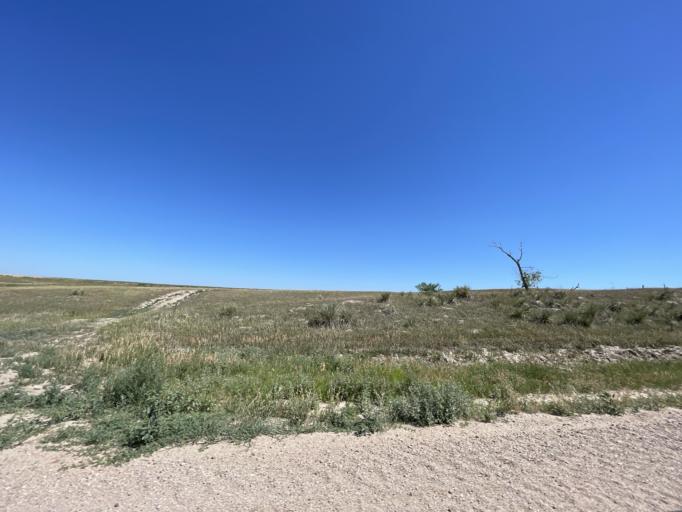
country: US
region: Nebraska
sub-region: Red Willow County
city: McCook
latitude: 40.4374
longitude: -100.6585
